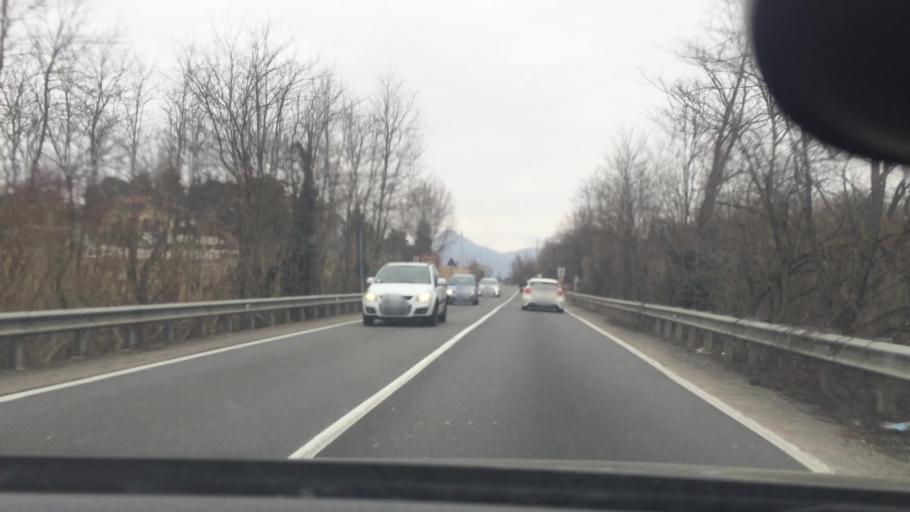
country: IT
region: Lombardy
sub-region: Provincia di Como
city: Nobile-Monguzzo
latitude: 45.7693
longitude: 9.2297
